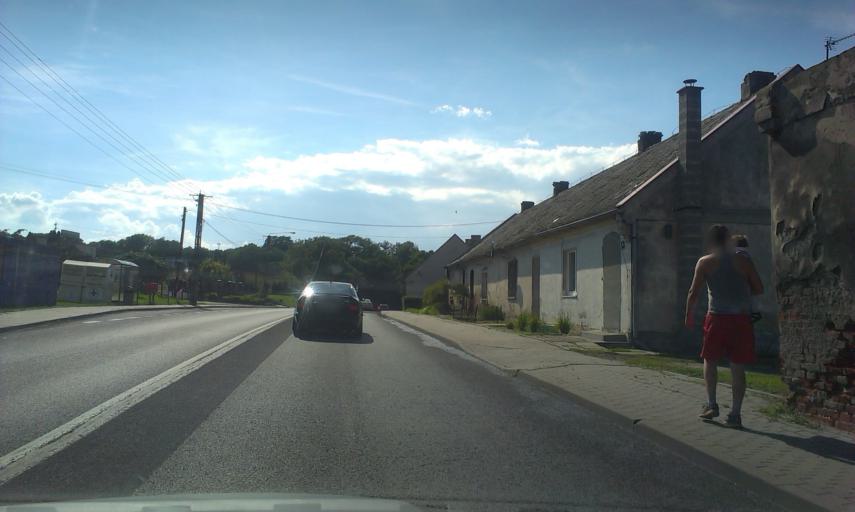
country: PL
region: Kujawsko-Pomorskie
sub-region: Powiat bydgoski
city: Sicienko
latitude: 53.1671
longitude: 17.7756
